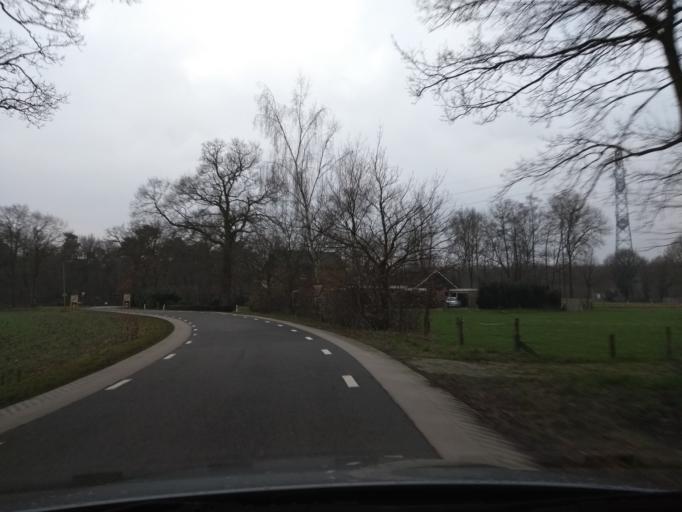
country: NL
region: Overijssel
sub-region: Gemeente Almelo
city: Almelo
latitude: 52.3158
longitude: 6.6945
